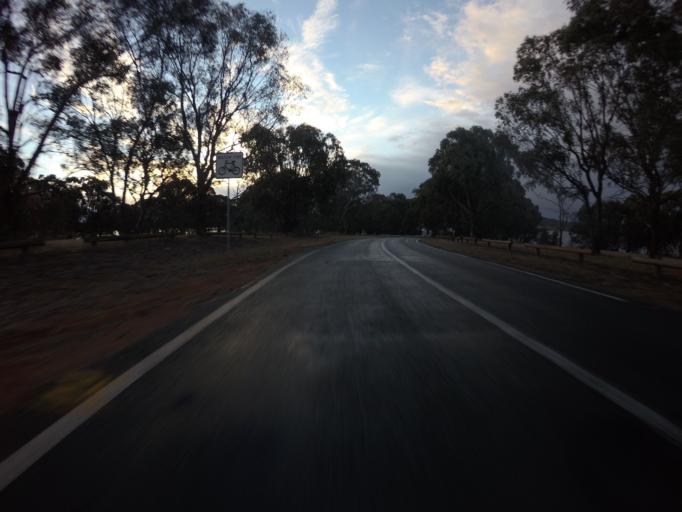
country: AU
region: Australian Capital Territory
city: Acton
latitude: -35.2977
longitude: 149.1084
